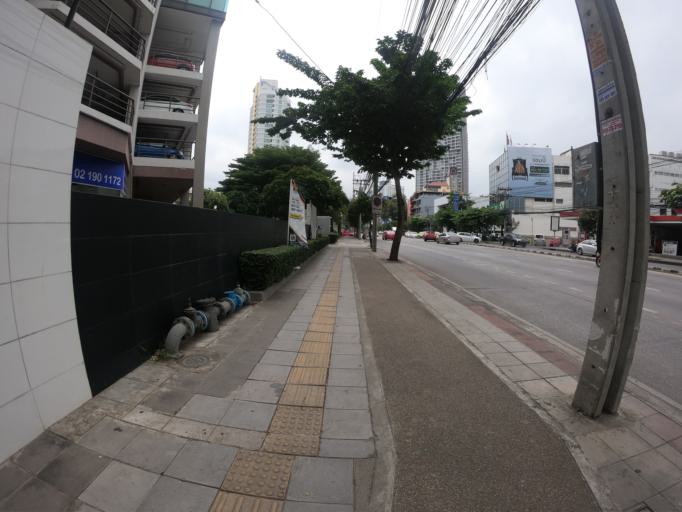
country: TH
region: Bangkok
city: Chatuchak
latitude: 13.8107
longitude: 100.5655
